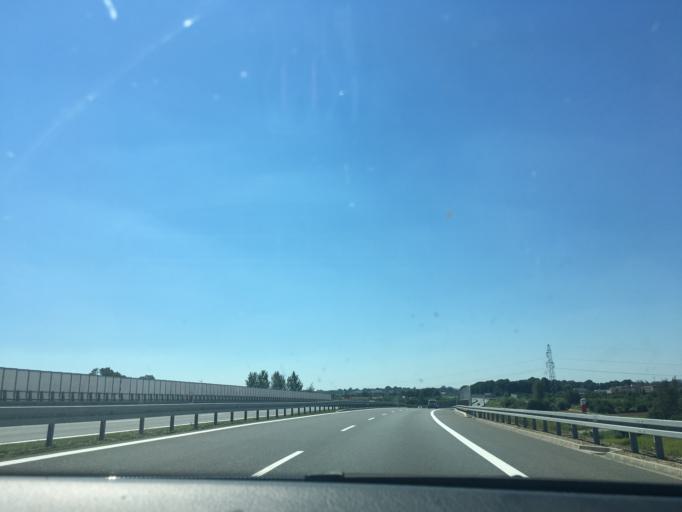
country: PL
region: Subcarpathian Voivodeship
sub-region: Powiat rzeszowski
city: Trzebownisko
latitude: 50.0659
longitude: 22.0529
